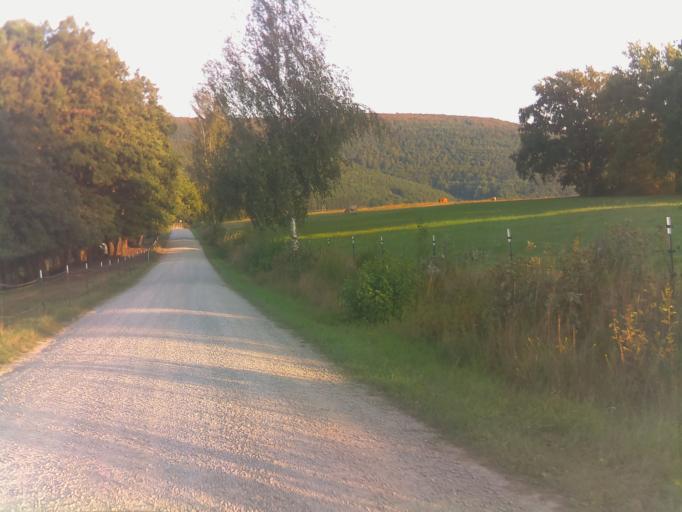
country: DE
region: Bavaria
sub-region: Regierungsbezirk Unterfranken
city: Burgsinn
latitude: 50.1582
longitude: 9.6364
